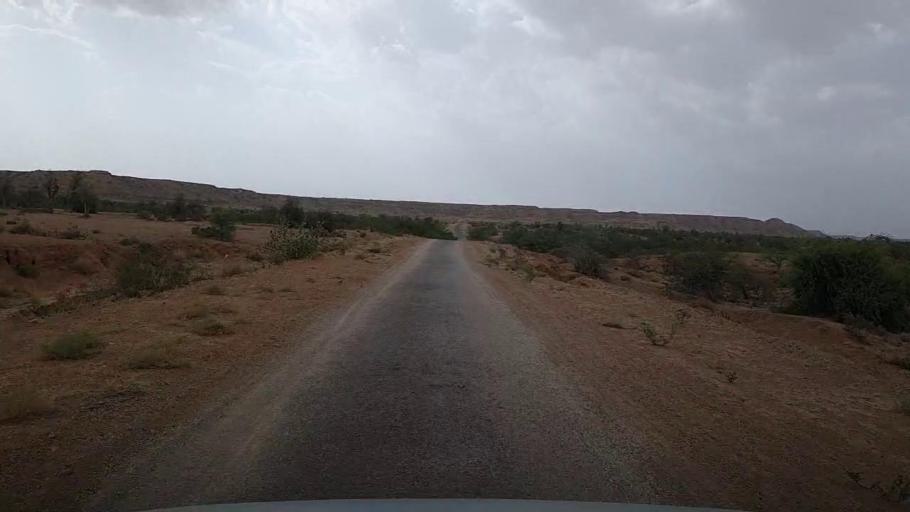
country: PK
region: Sindh
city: Jamshoro
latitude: 25.4140
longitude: 67.6988
